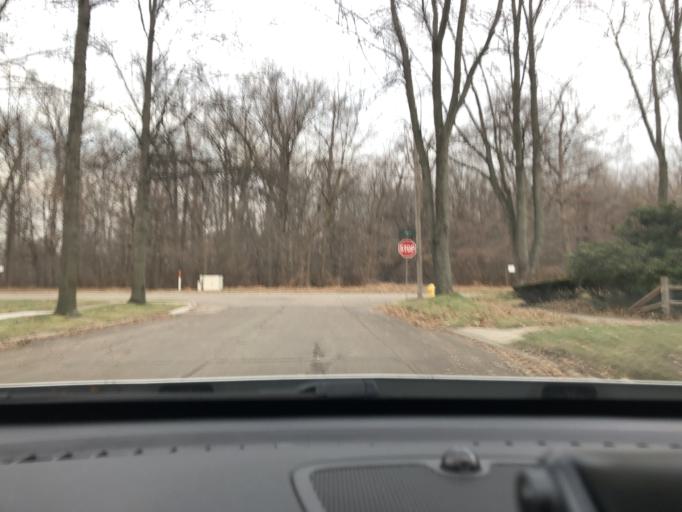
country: US
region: Michigan
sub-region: Wayne County
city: Allen Park
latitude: 42.2916
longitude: -83.2267
